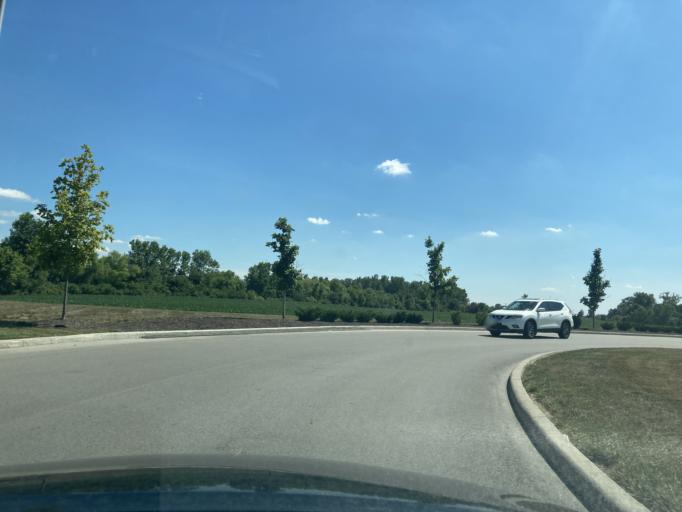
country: US
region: Indiana
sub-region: Hamilton County
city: Fishers
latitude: 39.9527
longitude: -86.0047
